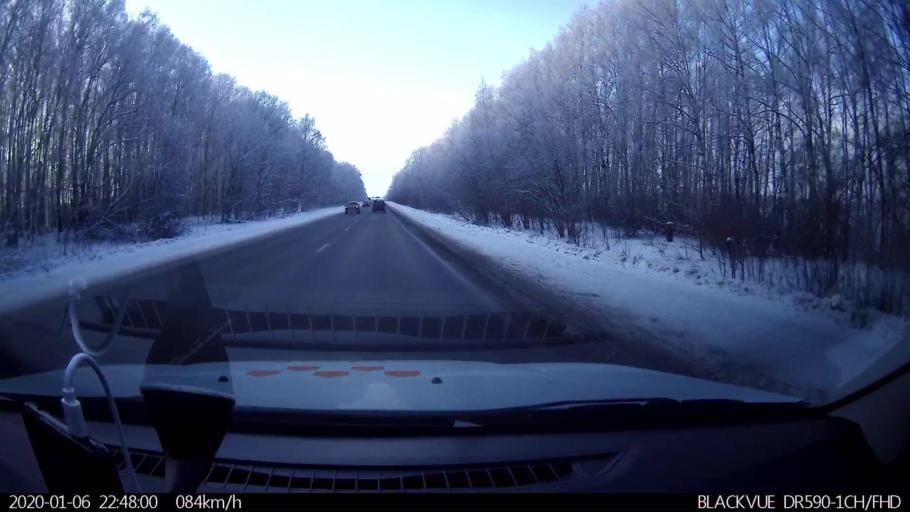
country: RU
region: Nizjnij Novgorod
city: Babino
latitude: 56.1420
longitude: 43.6636
